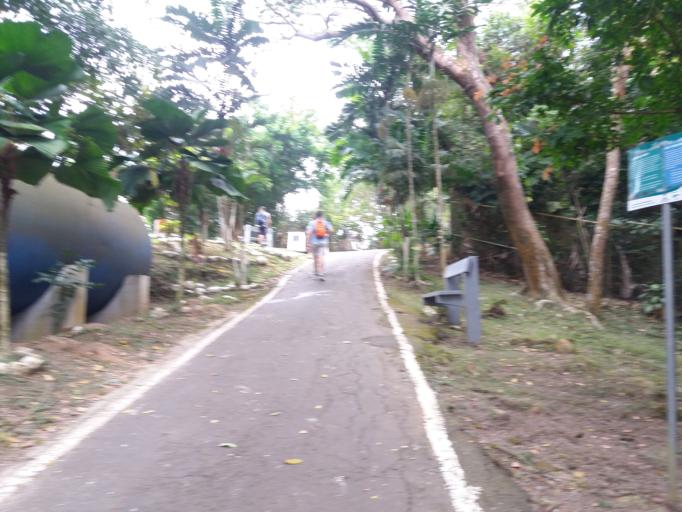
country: PA
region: Panama
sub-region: Distrito de Panama
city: Ancon
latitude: 8.9575
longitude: -79.5494
